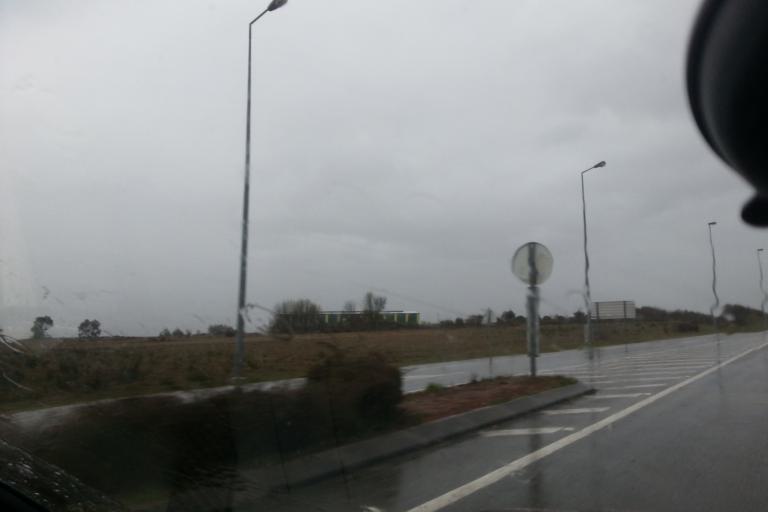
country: PT
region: Guarda
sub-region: Fornos de Algodres
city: Fornos de Algodres
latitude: 40.5352
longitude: -7.5701
